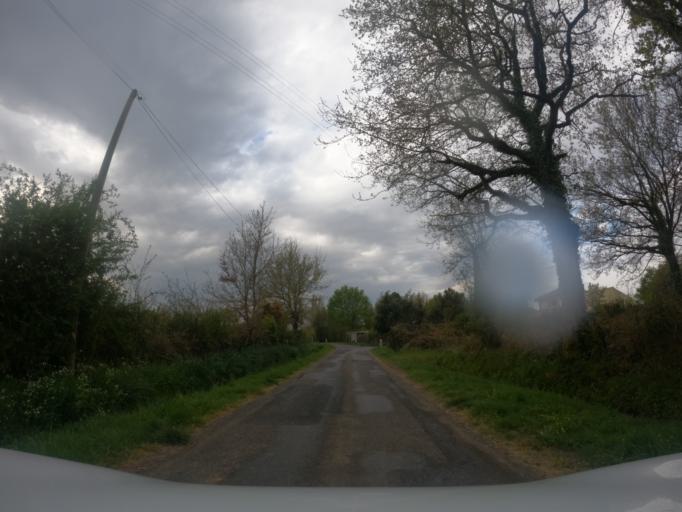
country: FR
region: Pays de la Loire
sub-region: Departement de la Vendee
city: Saint-Vincent-sur-Graon
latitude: 46.5395
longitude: -1.3652
